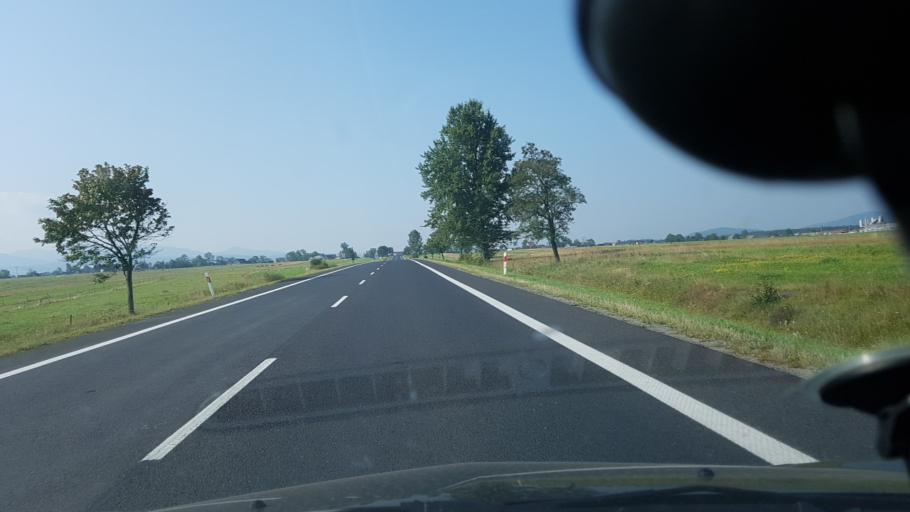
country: PL
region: Lesser Poland Voivodeship
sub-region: Powiat nowotarski
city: Chyzne
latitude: 49.4344
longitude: 19.6788
